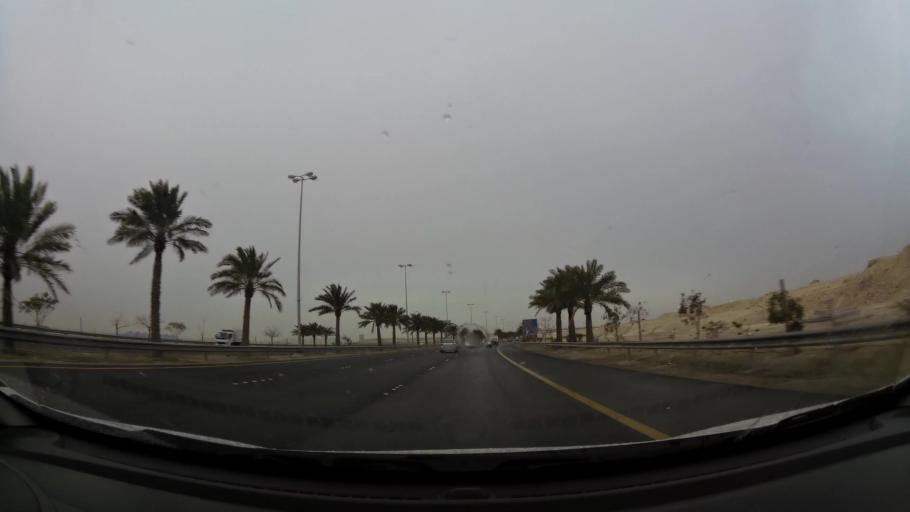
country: BH
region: Central Governorate
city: Dar Kulayb
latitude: 26.0901
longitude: 50.5151
